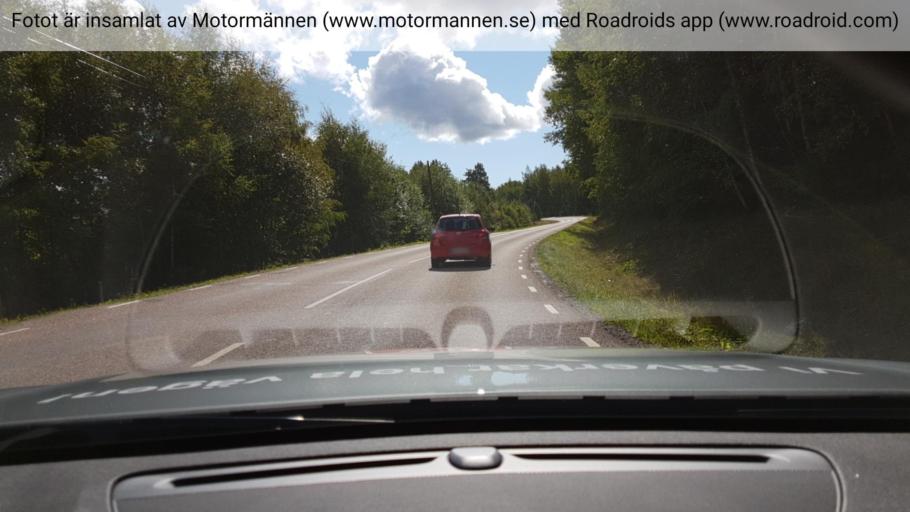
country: SE
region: Soedermanland
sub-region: Strangnas Kommun
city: Stallarholmen
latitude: 59.3535
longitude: 17.2163
